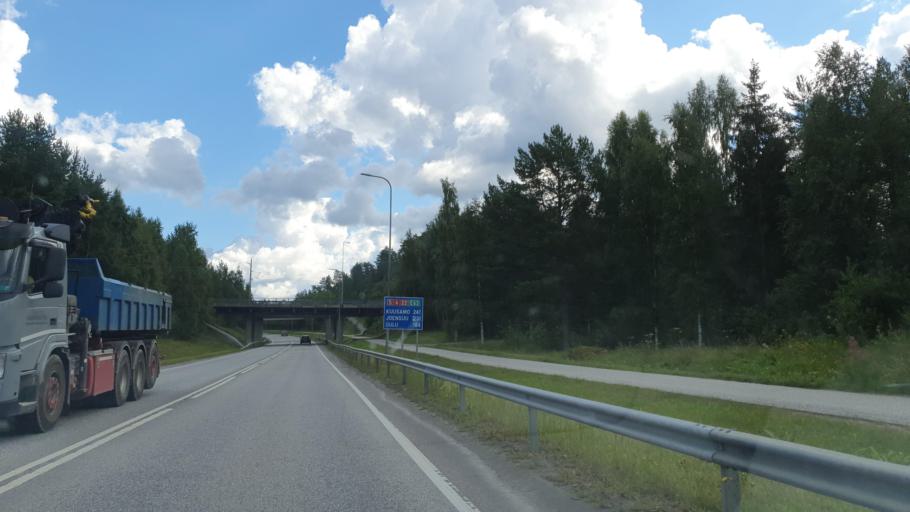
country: FI
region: Kainuu
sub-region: Kajaani
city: Kajaani
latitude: 64.2179
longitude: 27.6961
